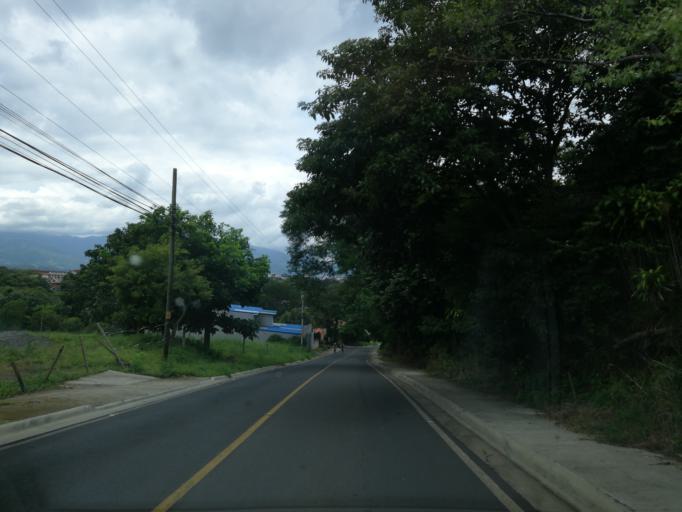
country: CR
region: Alajuela
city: Alajuela
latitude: 10.0244
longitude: -84.1968
